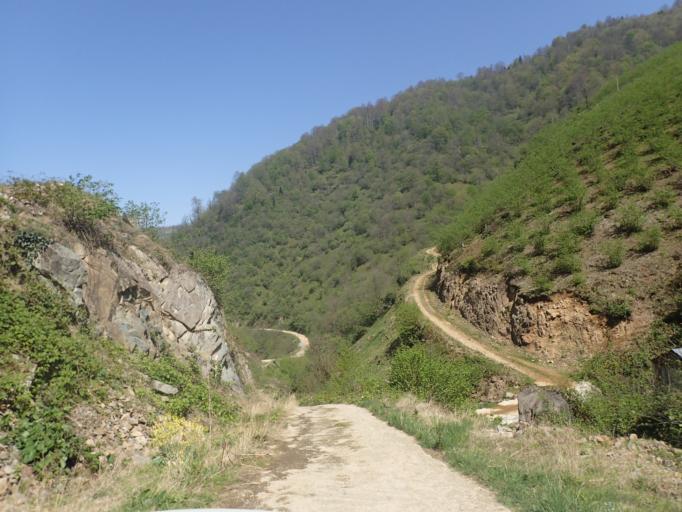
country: TR
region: Ordu
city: Kabaduz
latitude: 40.7368
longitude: 37.8920
